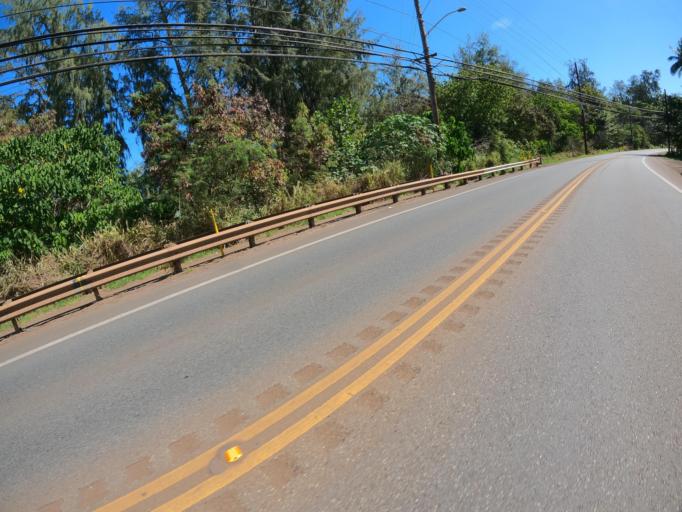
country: US
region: Hawaii
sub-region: Honolulu County
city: Kahuku
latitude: 21.6720
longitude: -157.9404
